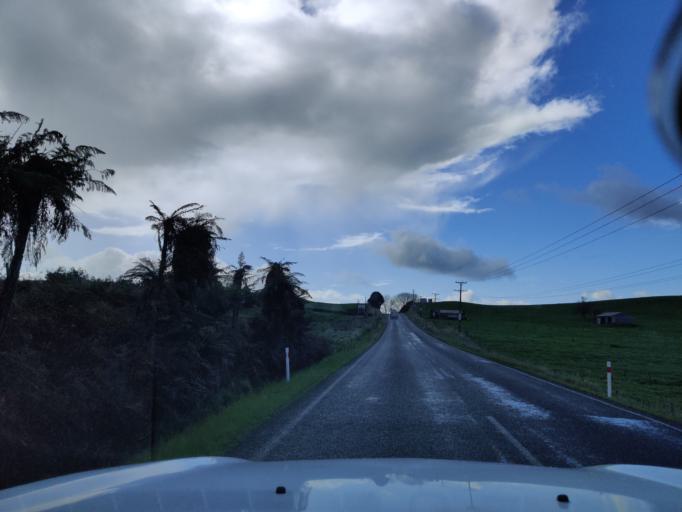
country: NZ
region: Waikato
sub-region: Waikato District
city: Ngaruawahia
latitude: -37.5773
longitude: 175.2307
